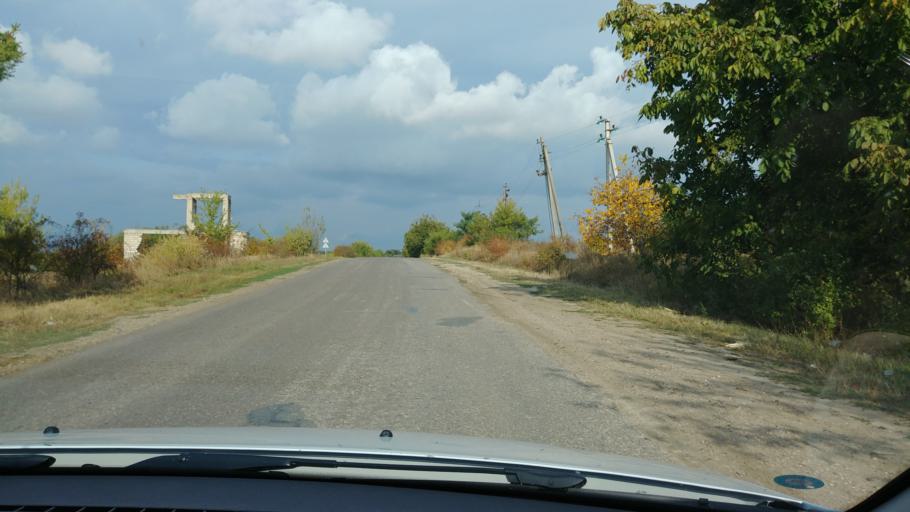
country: MD
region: Criuleni
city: Criuleni
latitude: 47.2146
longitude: 29.0701
